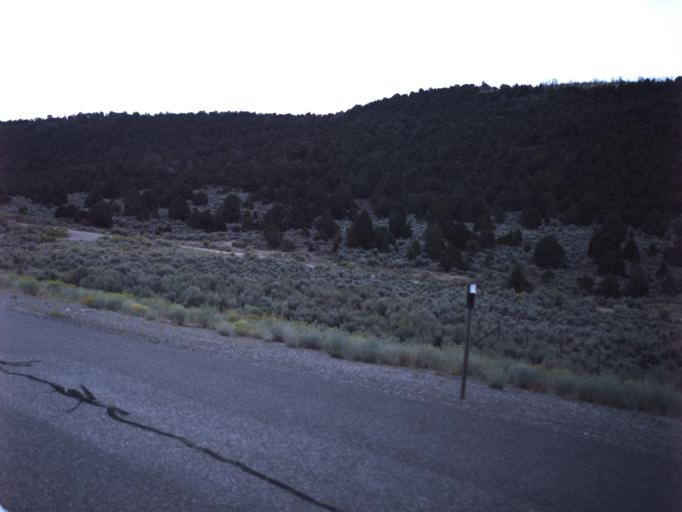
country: US
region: Utah
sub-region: Sevier County
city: Monroe
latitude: 38.5509
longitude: -112.4020
